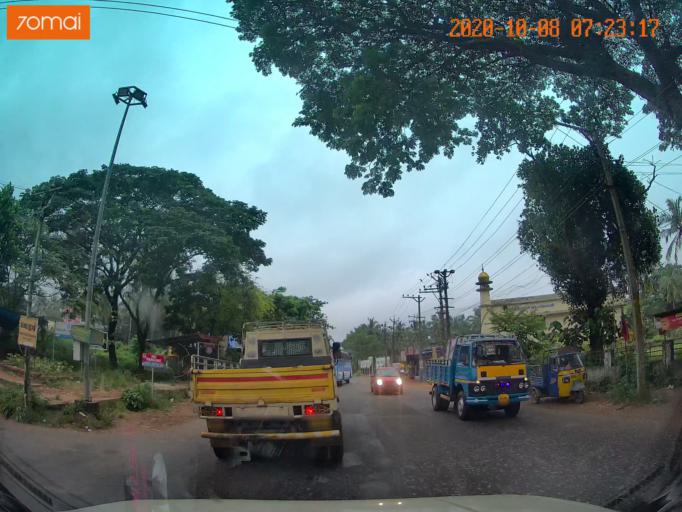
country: IN
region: Kerala
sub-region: Malappuram
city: Tirur
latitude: 10.8679
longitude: 76.0450
